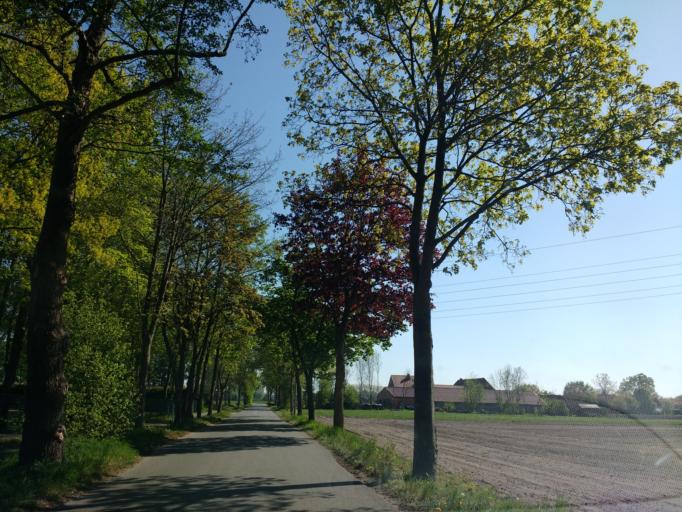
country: DE
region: North Rhine-Westphalia
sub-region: Regierungsbezirk Detmold
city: Delbruck
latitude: 51.7510
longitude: 8.5967
